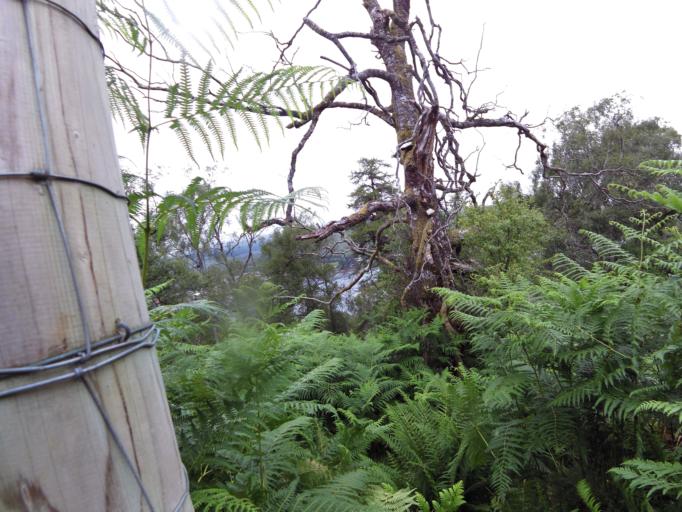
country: GB
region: Scotland
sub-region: Highland
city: Fort William
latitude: 56.8310
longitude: -5.1297
